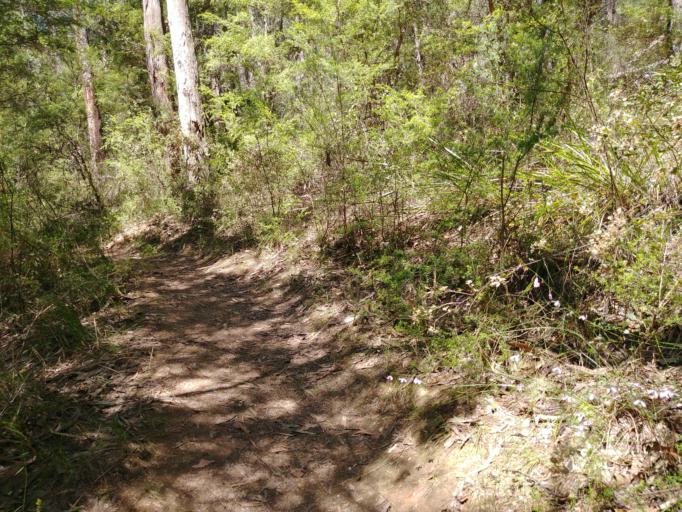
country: AU
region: Victoria
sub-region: Cardinia
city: Gembrook
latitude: -37.8980
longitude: 145.5722
